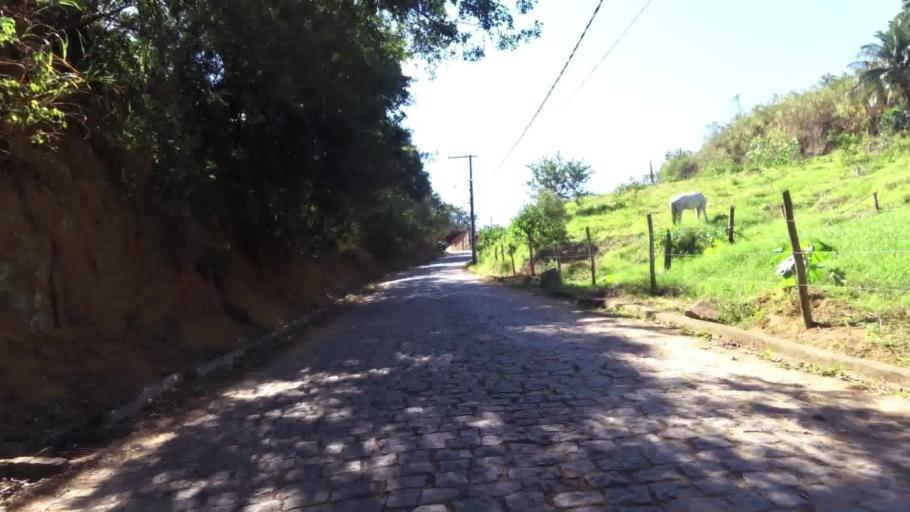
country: BR
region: Espirito Santo
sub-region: Rio Novo Do Sul
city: Rio Novo do Sul
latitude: -20.8681
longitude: -40.9319
